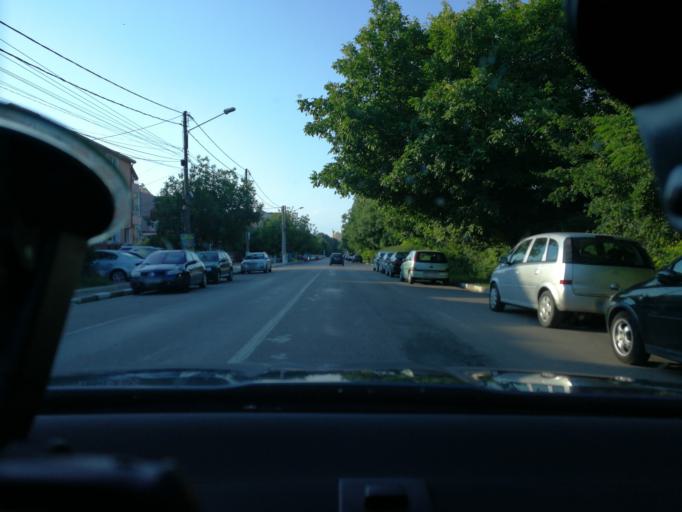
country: RO
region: Constanta
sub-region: Oras Eforie
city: Eforie Nord
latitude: 44.0713
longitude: 28.6297
